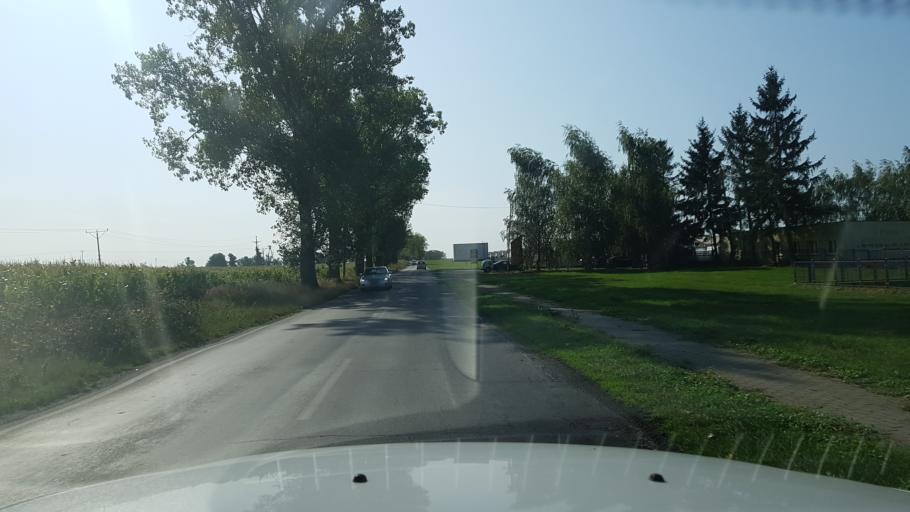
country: PL
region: West Pomeranian Voivodeship
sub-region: Powiat stargardzki
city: Stargard Szczecinski
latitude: 53.2764
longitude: 15.0818
